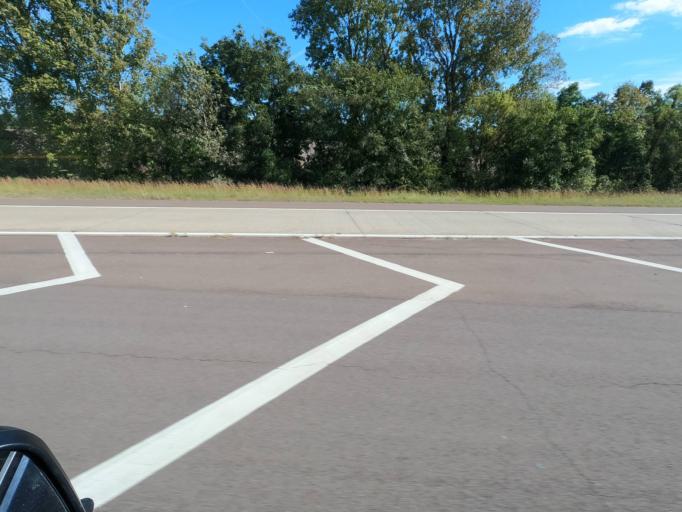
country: US
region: Tennessee
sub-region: Dyer County
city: Dyersburg
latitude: 36.0289
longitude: -89.3401
